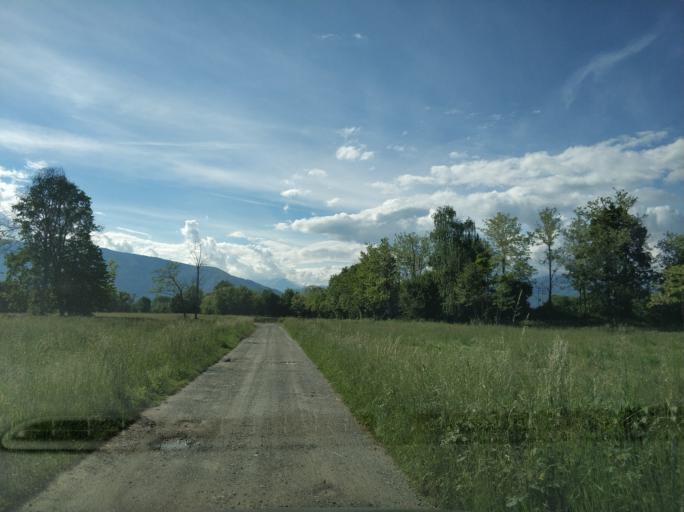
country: IT
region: Piedmont
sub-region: Provincia di Torino
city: Nole
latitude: 45.2284
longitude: 7.5740
